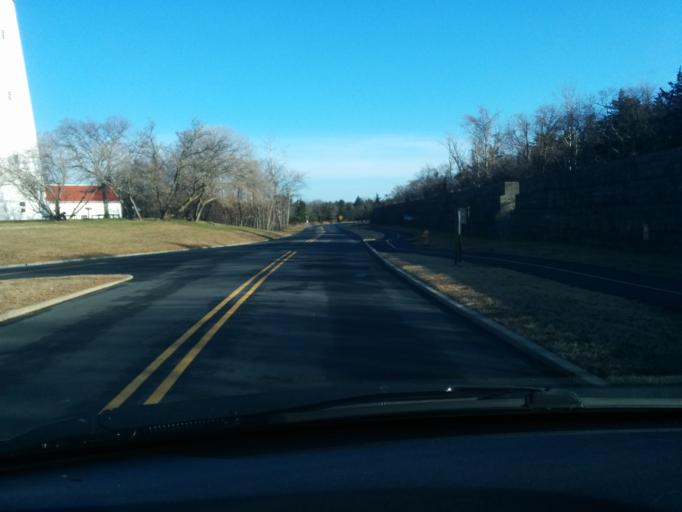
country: US
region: New Jersey
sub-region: Monmouth County
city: Highlands
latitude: 40.4611
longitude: -74.0021
